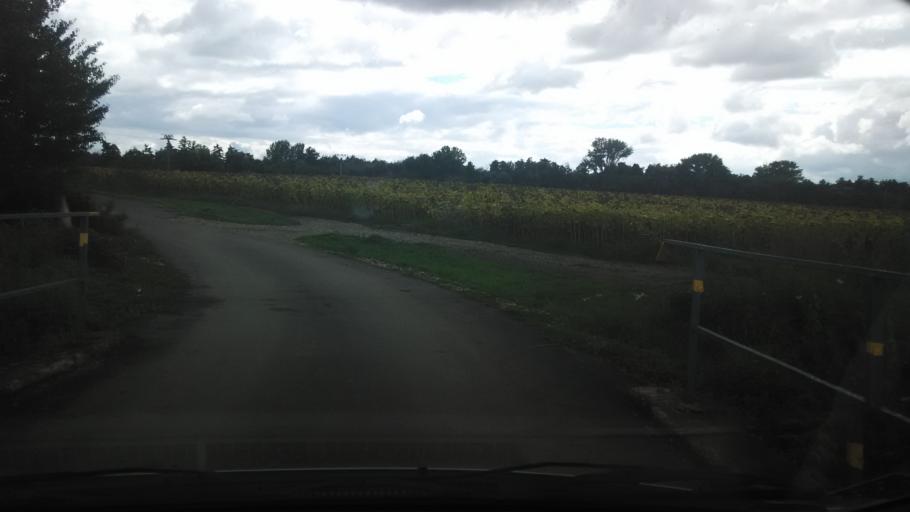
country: SK
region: Nitriansky
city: Levice
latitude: 48.1934
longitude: 18.5225
